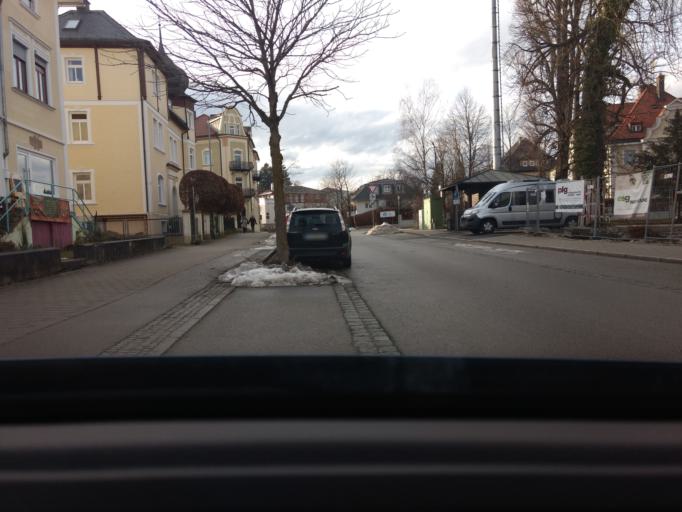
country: DE
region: Bavaria
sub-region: Upper Bavaria
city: Traunstein
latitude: 47.8662
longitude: 12.6412
